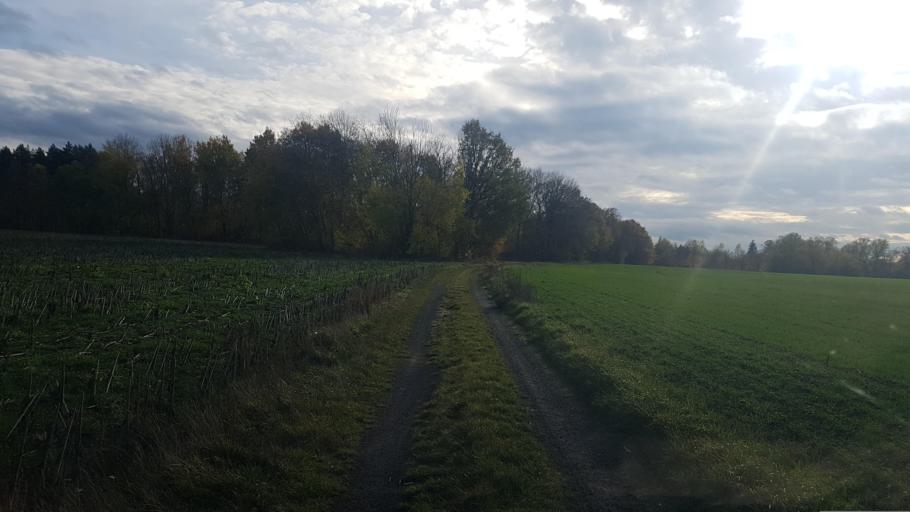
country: DE
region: Brandenburg
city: Wiesenburg
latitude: 52.0783
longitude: 12.4639
